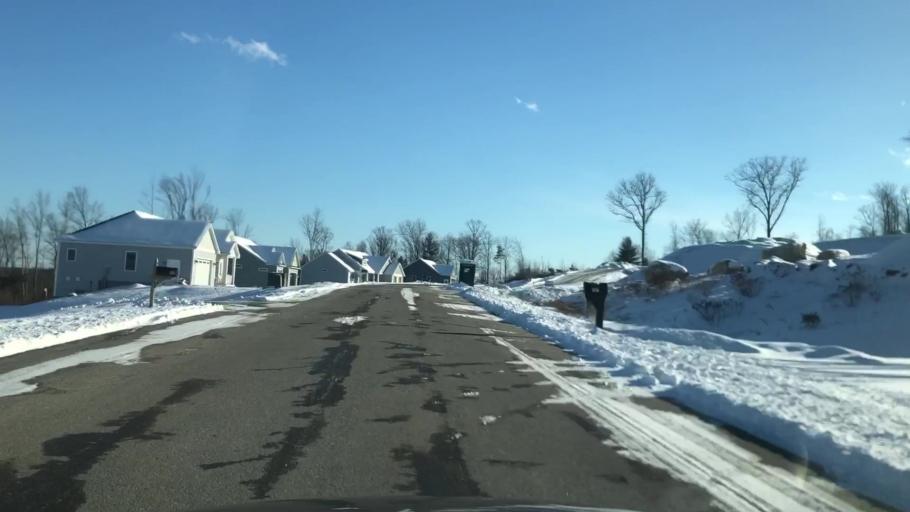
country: US
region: New Hampshire
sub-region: Hillsborough County
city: Wilton
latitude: 42.8059
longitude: -71.7110
